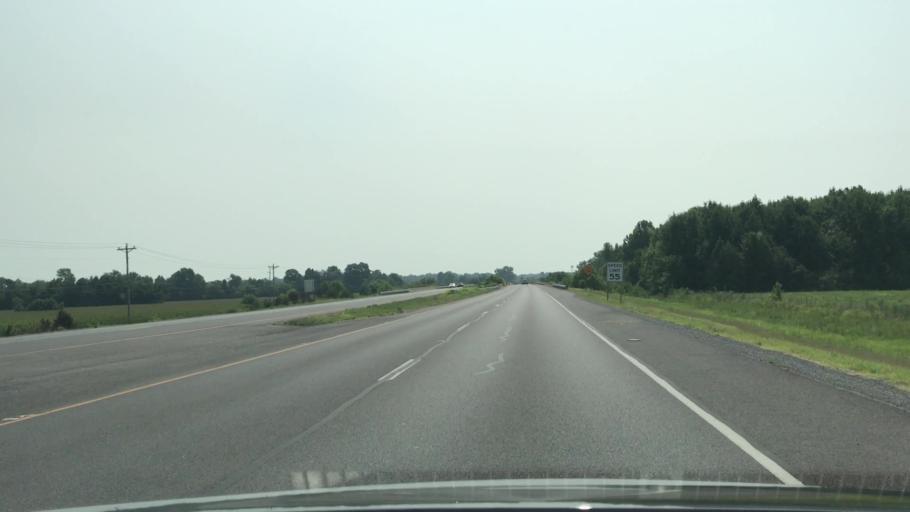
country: US
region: Kentucky
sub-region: Graves County
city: Mayfield
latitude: 36.7144
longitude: -88.6184
